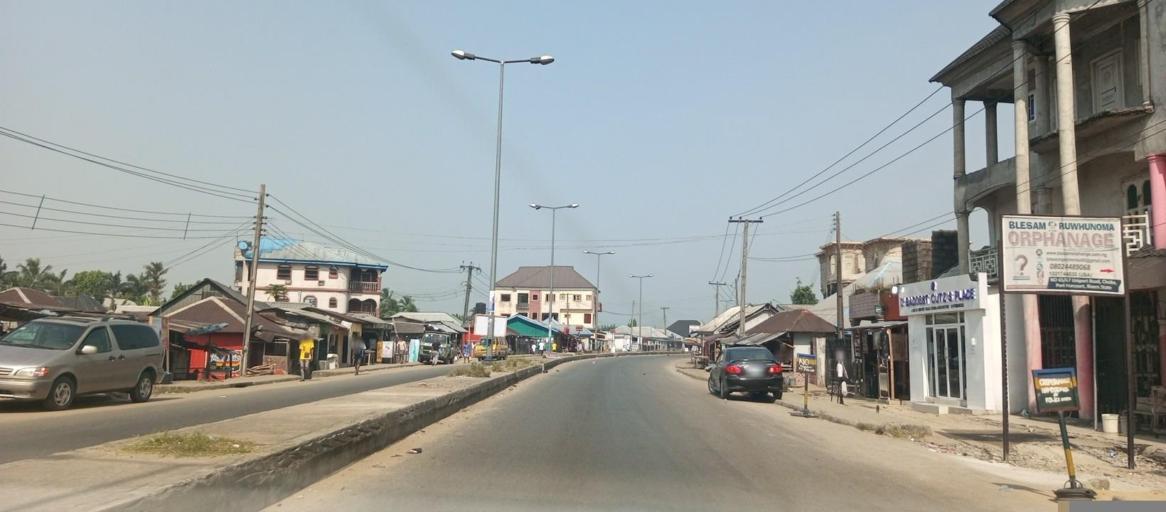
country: NG
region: Rivers
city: Emuoha
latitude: 4.8854
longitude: 6.9023
